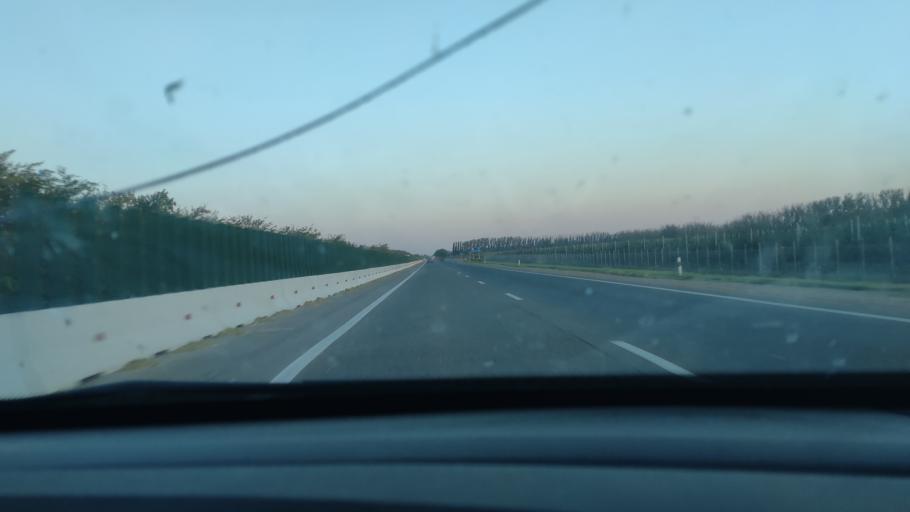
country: RU
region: Krasnodarskiy
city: Timashevsk
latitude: 45.5782
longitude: 38.9183
